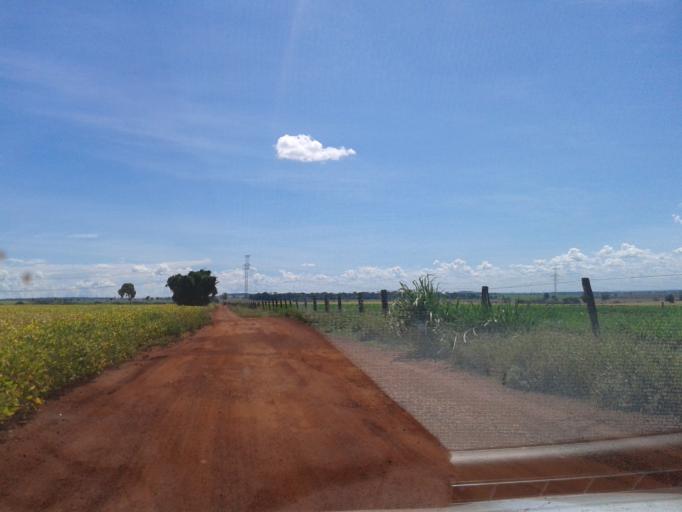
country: BR
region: Minas Gerais
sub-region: Capinopolis
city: Capinopolis
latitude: -18.7040
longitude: -49.7784
